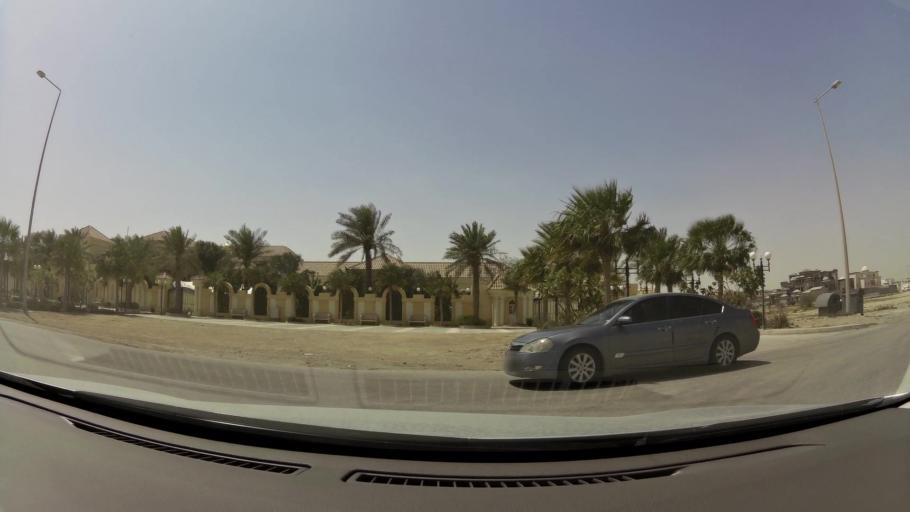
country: QA
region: Baladiyat Umm Salal
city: Umm Salal Muhammad
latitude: 25.3967
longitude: 51.4444
